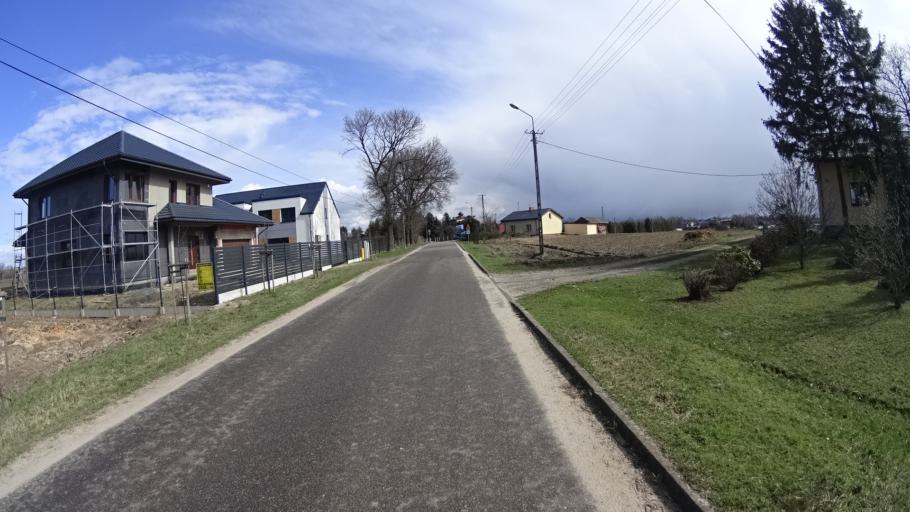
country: PL
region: Masovian Voivodeship
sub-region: Powiat warszawski zachodni
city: Jozefow
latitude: 52.2057
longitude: 20.6864
